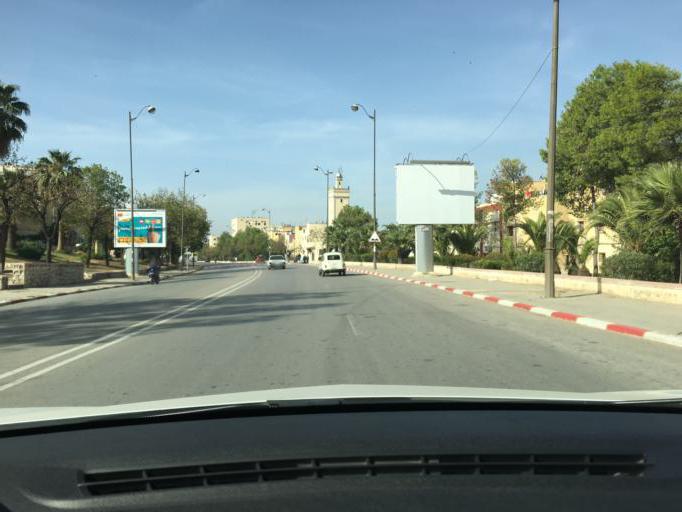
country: MA
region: Fes-Boulemane
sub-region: Fes
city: Fes
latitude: 34.0409
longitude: -5.0176
